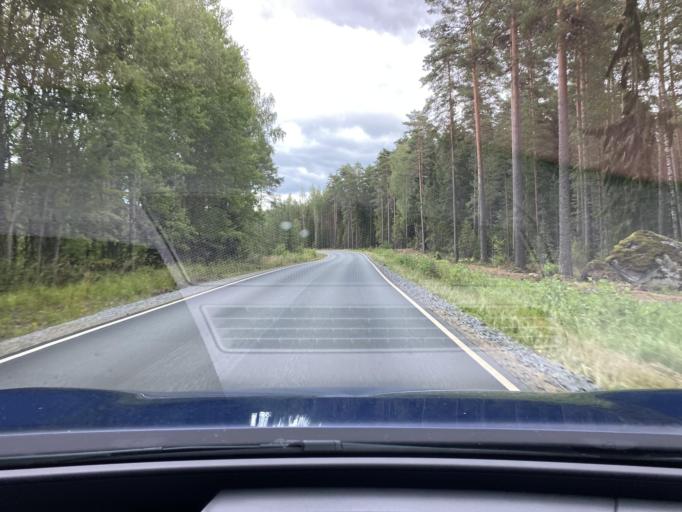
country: FI
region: Pirkanmaa
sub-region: Lounais-Pirkanmaa
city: Vammala
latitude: 61.3007
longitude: 22.9652
